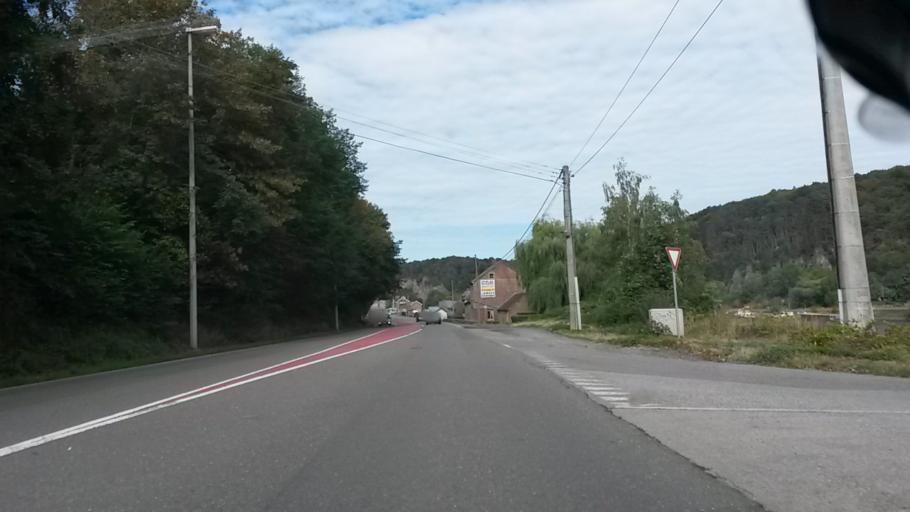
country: BE
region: Wallonia
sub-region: Province de Namur
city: Noville-les-Bois
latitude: 50.4766
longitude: 4.9742
